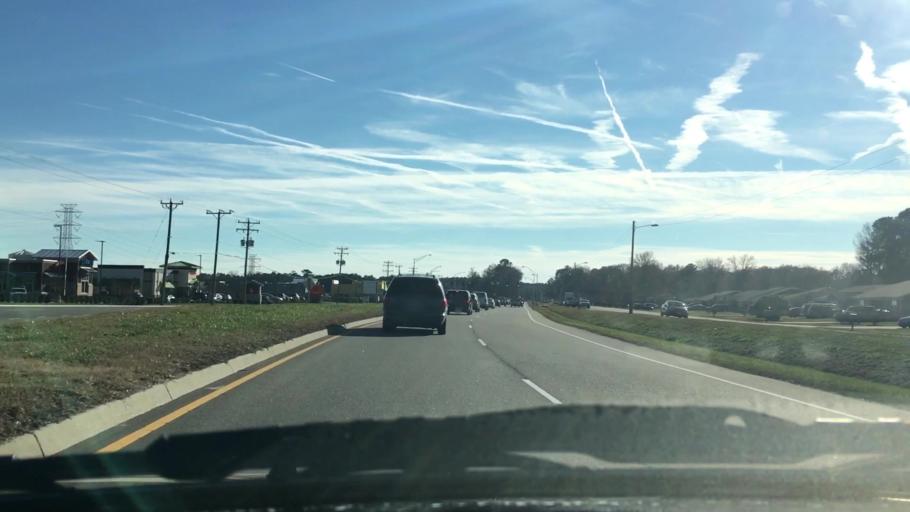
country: US
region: Virginia
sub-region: City of Portsmouth
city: Portsmouth Heights
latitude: 36.8767
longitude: -76.4231
